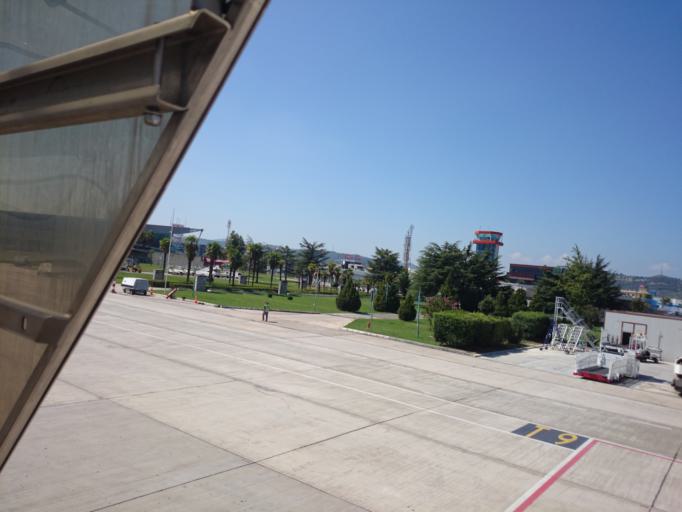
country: AL
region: Durres
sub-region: Rrethi i Krujes
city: Nikel
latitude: 41.4214
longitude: 19.7148
